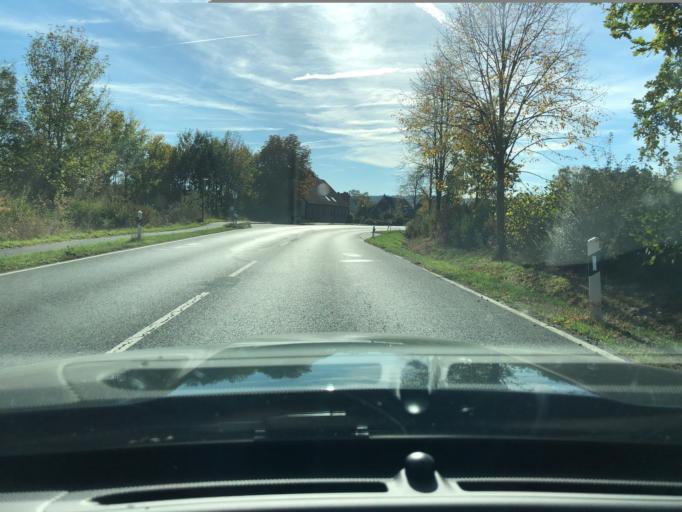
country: DE
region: Lower Saxony
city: Hagen
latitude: 52.2498
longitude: 7.9847
